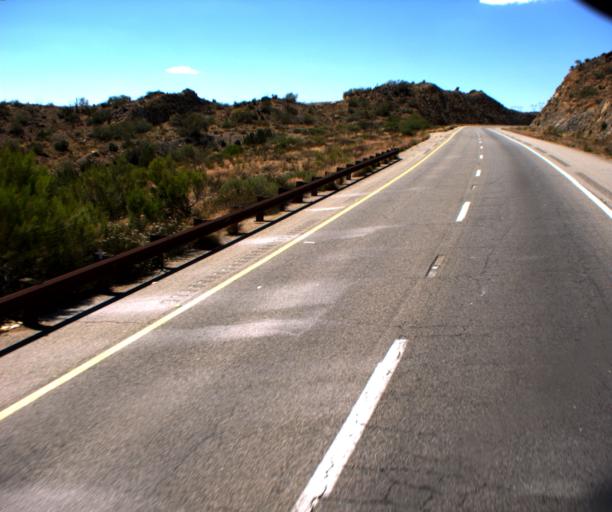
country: US
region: Arizona
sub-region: Yavapai County
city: Bagdad
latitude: 34.4572
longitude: -113.2909
